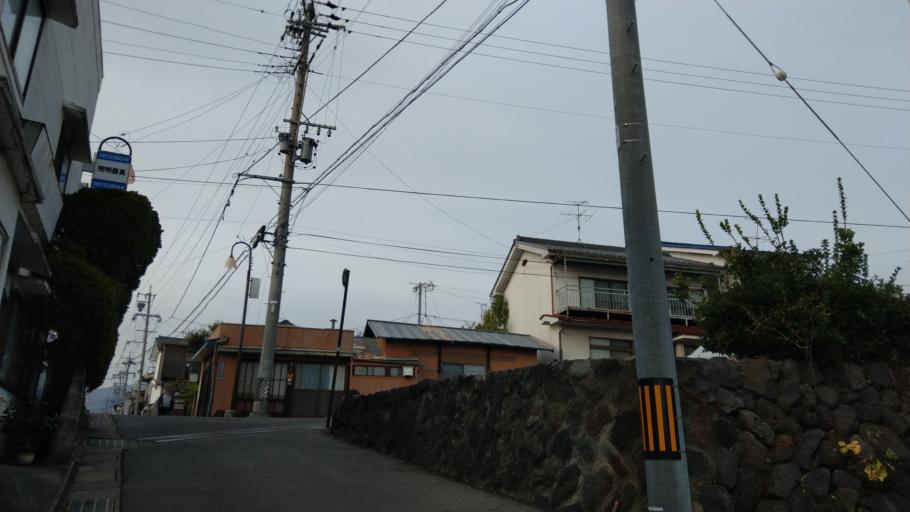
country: JP
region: Nagano
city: Komoro
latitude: 36.3226
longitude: 138.4295
